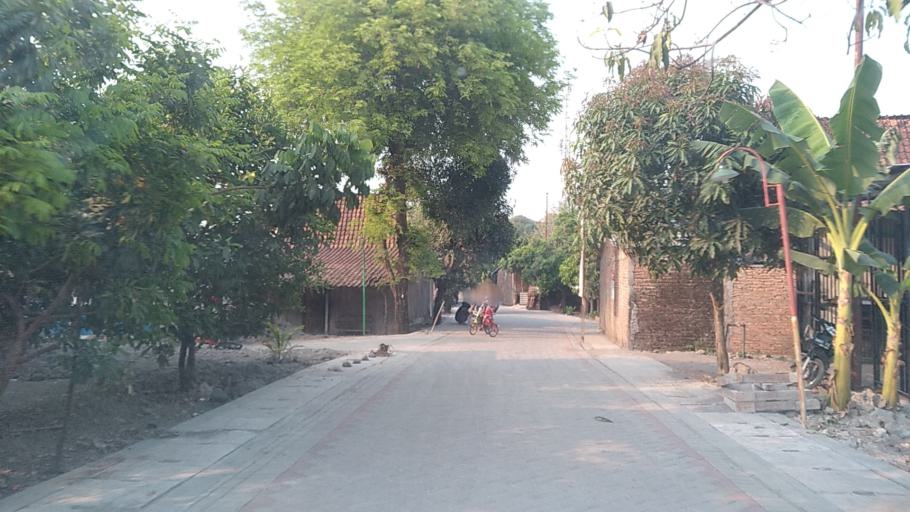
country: ID
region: Central Java
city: Mranggen
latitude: -7.0632
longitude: 110.4848
